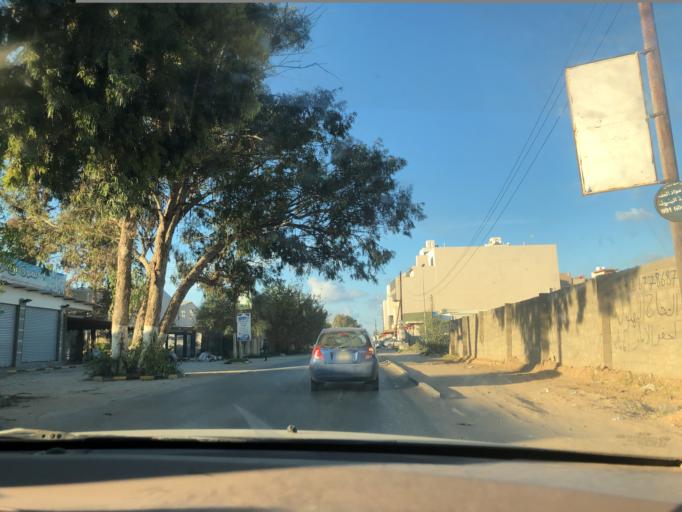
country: LY
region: Tripoli
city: Tagiura
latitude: 32.8569
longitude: 13.2789
